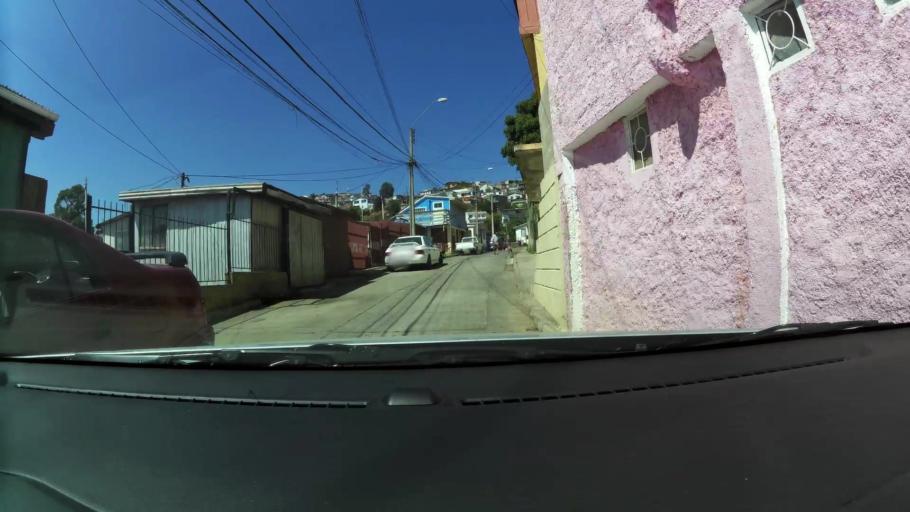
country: CL
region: Valparaiso
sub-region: Provincia de Valparaiso
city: Valparaiso
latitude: -33.0446
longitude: -71.6460
